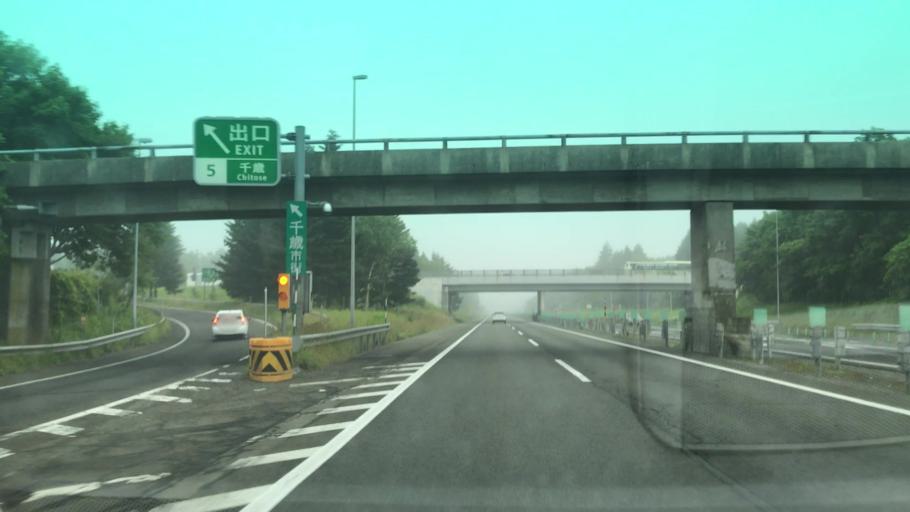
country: JP
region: Hokkaido
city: Chitose
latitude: 42.8130
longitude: 141.6206
